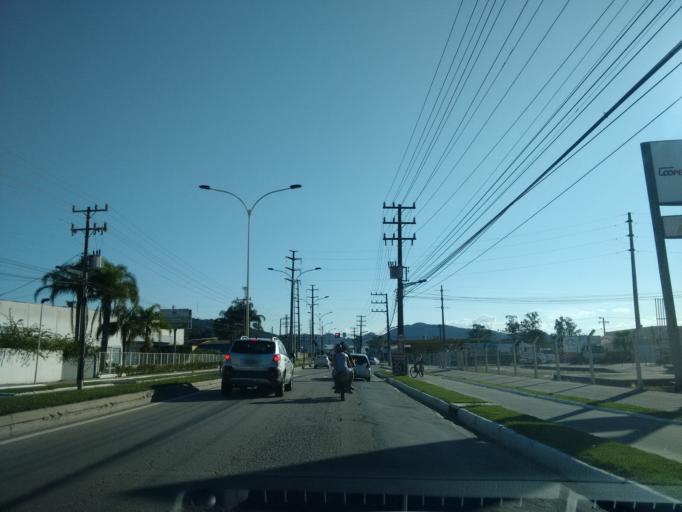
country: BR
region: Santa Catarina
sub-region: Itajai
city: Itajai
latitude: -26.8910
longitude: -48.7129
